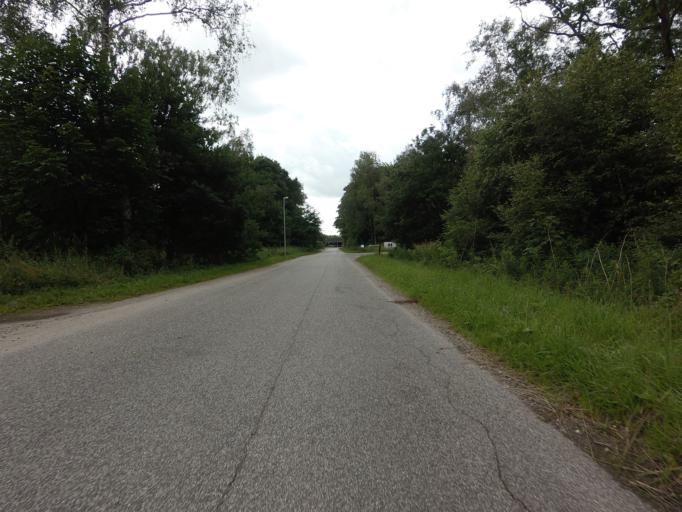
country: DK
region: Central Jutland
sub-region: Randers Kommune
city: Langa
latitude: 56.3868
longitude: 9.8995
